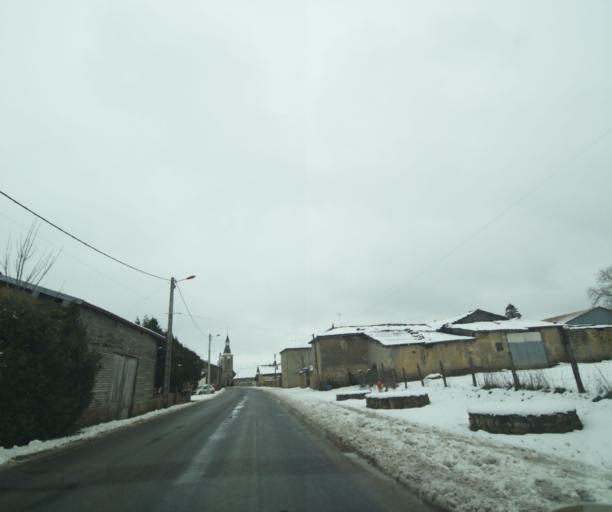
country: FR
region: Champagne-Ardenne
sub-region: Departement de la Haute-Marne
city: Montier-en-Der
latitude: 48.4221
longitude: 4.8188
